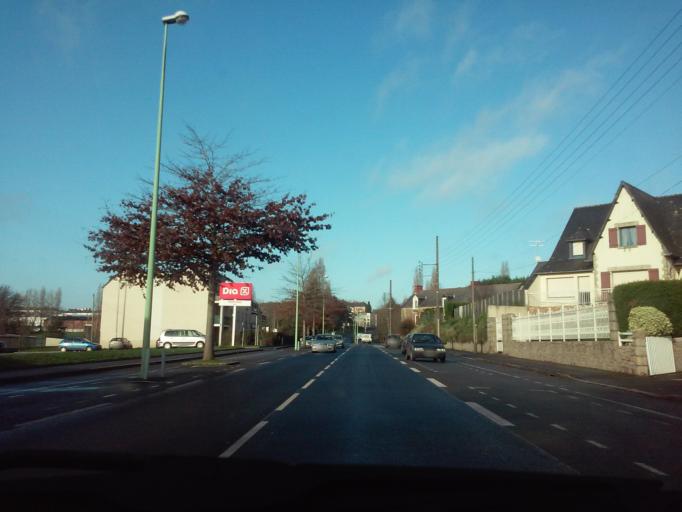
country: FR
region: Brittany
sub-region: Departement d'Ille-et-Vilaine
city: Fougeres
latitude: 48.3396
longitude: -1.1939
